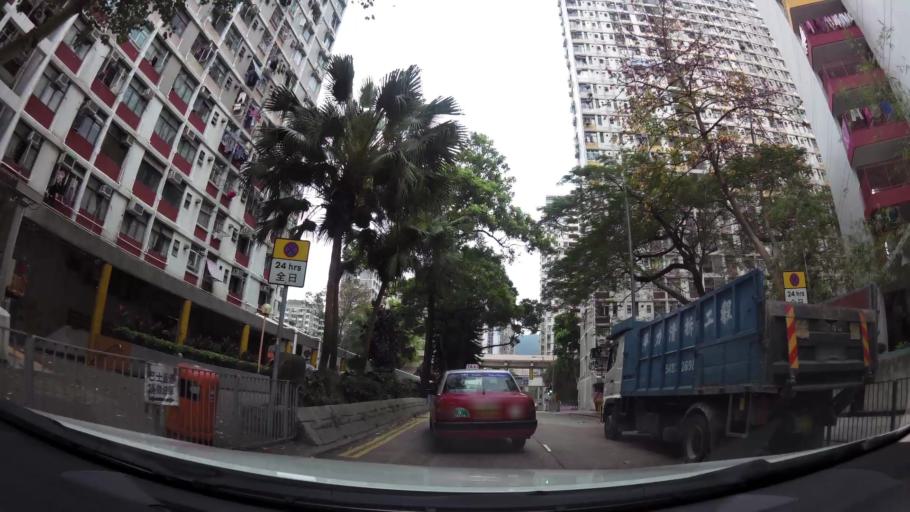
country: HK
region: Kowloon City
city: Kowloon
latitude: 22.3325
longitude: 114.1928
